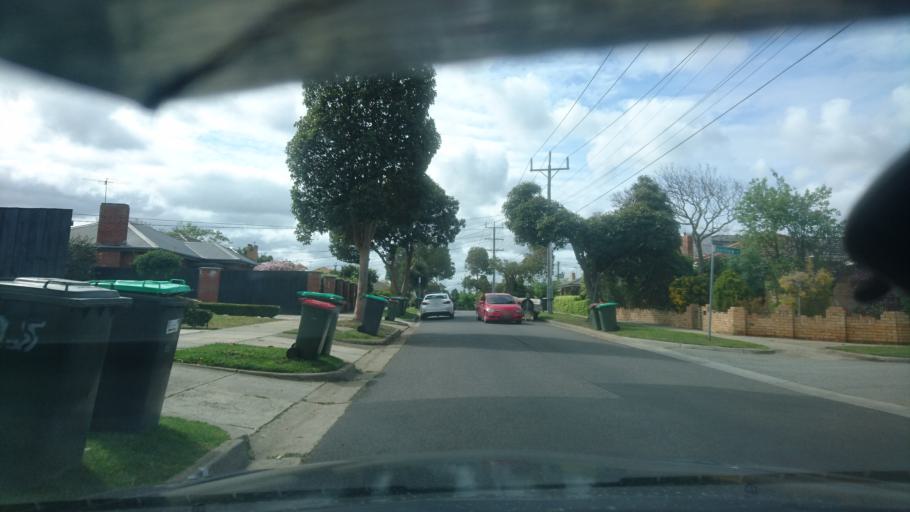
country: AU
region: Victoria
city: Murrumbeena
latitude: -37.9073
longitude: 145.0590
